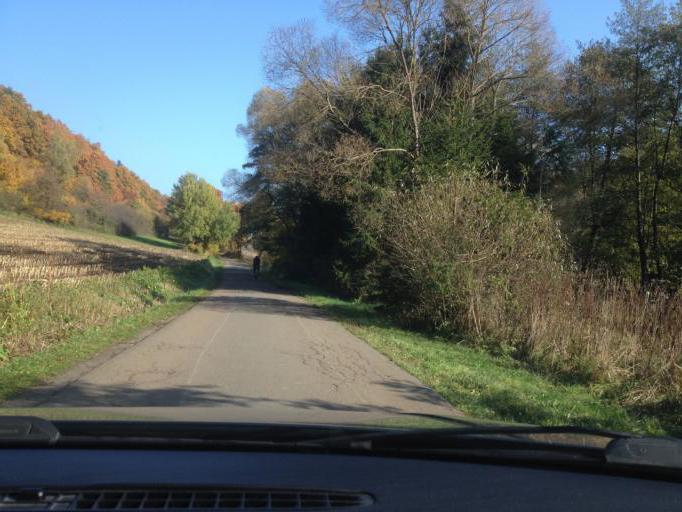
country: DE
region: Saarland
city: Sankt Wendel
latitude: 49.4919
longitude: 7.1825
